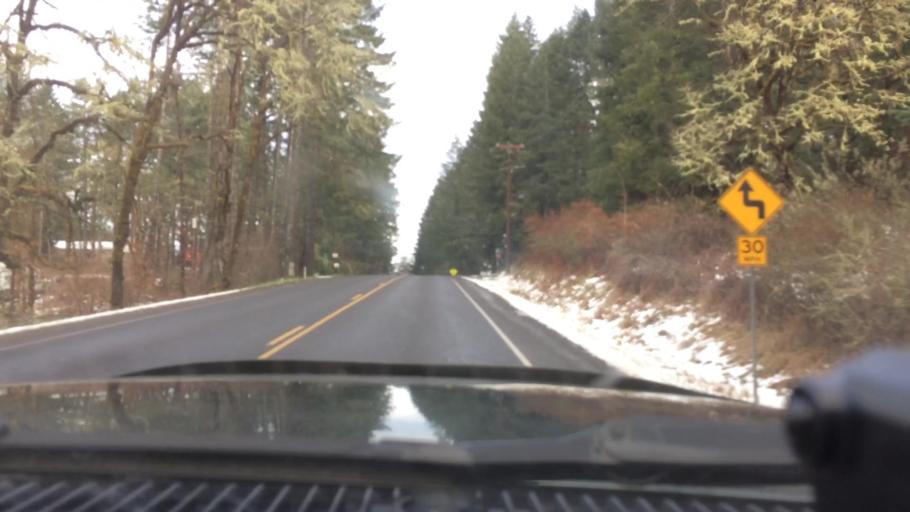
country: US
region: Oregon
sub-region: Lane County
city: Veneta
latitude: 44.1363
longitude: -123.3535
